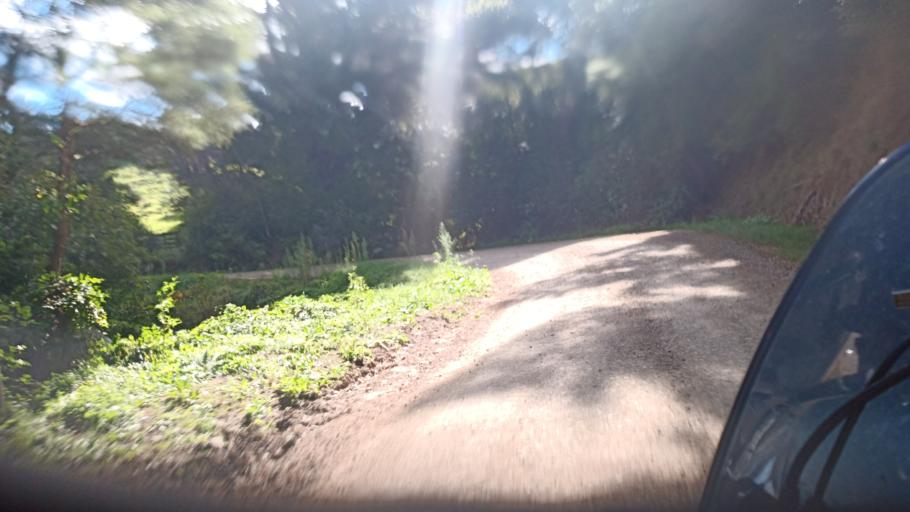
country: NZ
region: Gisborne
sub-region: Gisborne District
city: Gisborne
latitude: -38.4211
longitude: 177.7066
